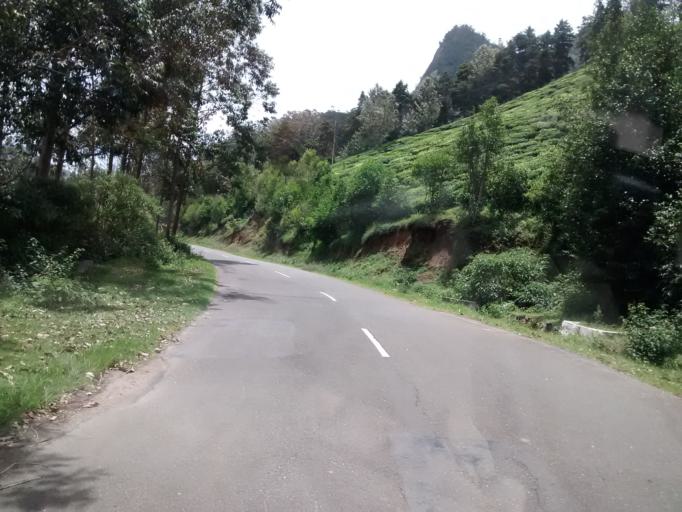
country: IN
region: Kerala
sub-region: Idukki
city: Munnar
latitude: 10.1353
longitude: 77.1775
